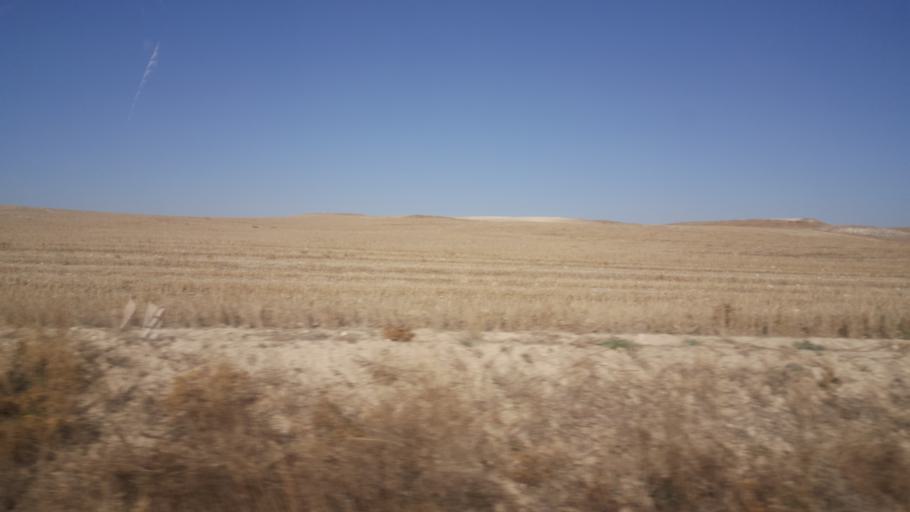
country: TR
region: Konya
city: Celtik
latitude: 39.0910
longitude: 32.0622
